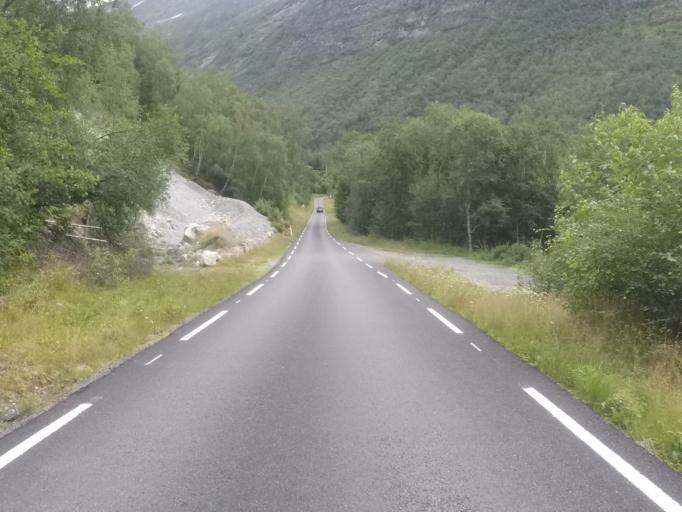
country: NO
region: Sogn og Fjordane
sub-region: Stryn
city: Stryn
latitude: 61.8036
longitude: 7.0068
